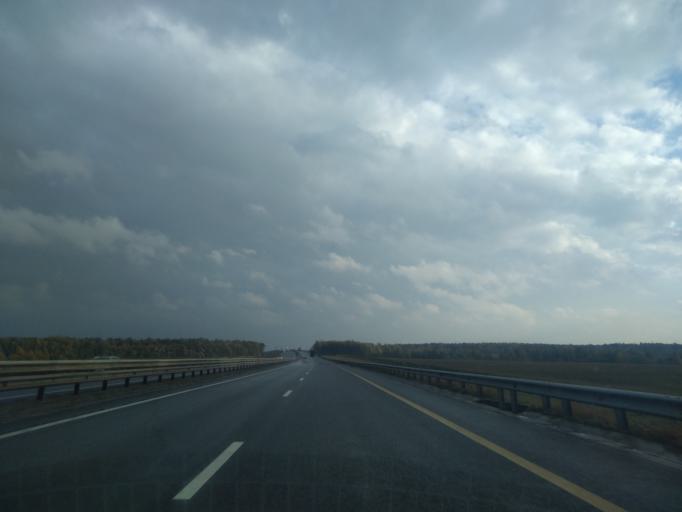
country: RU
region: Lipetsk
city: Yelets
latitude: 52.6014
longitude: 38.6689
